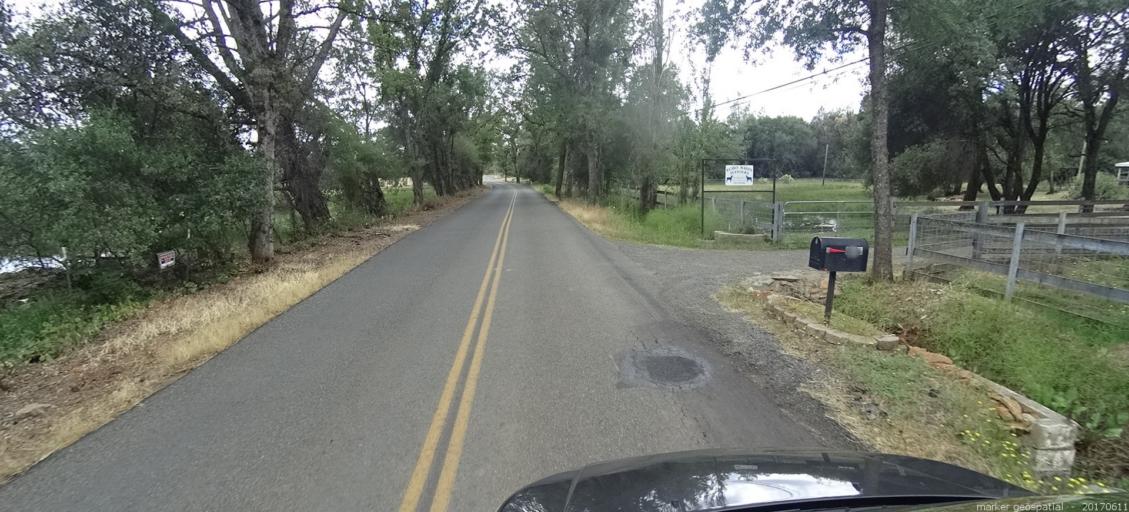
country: US
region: California
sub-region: Butte County
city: Oroville
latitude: 39.6306
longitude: -121.5287
